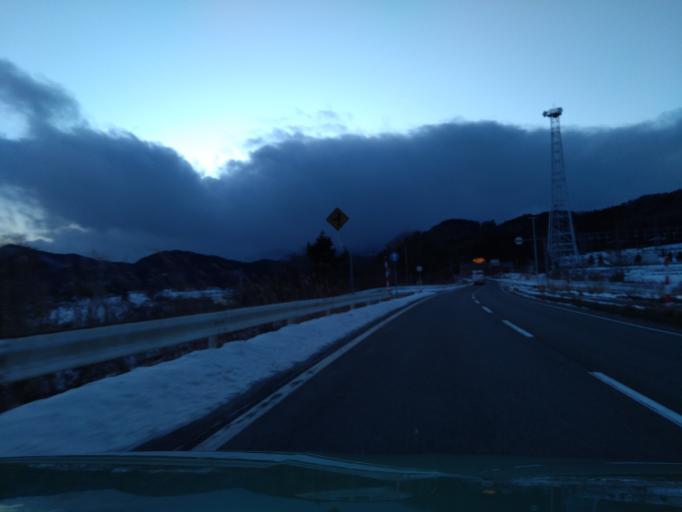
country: JP
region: Iwate
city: Shizukuishi
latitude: 39.6924
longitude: 140.9327
